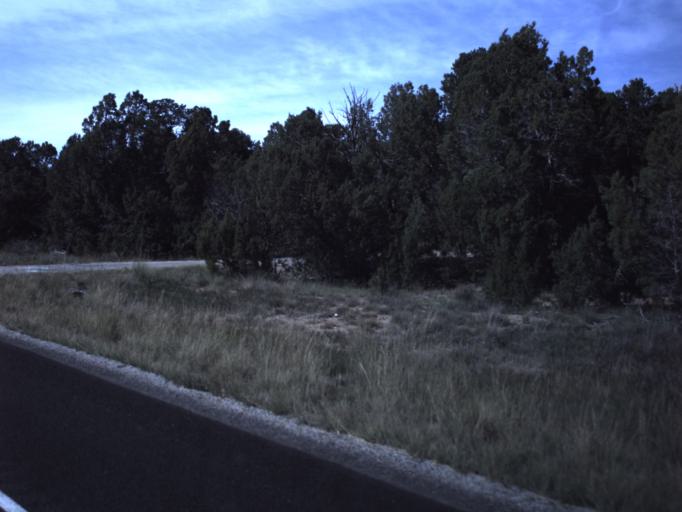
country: US
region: Utah
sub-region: San Juan County
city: Monticello
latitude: 37.8588
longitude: -109.2023
